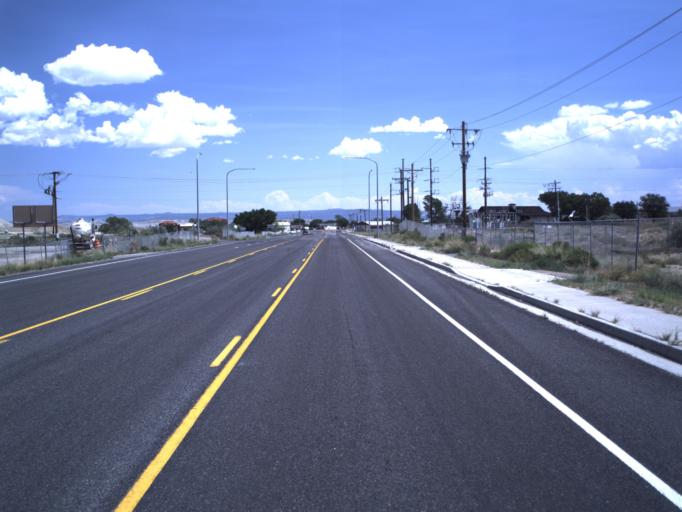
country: US
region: Utah
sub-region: Emery County
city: Huntington
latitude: 39.3371
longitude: -110.9709
